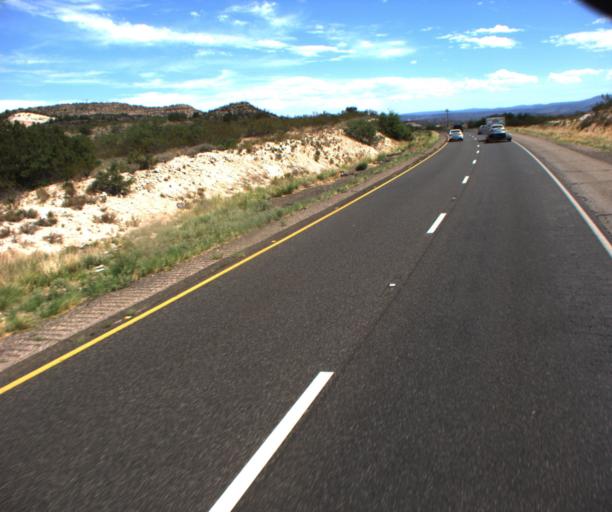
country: US
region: Arizona
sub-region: Yavapai County
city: Lake Montezuma
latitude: 34.6256
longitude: -111.8374
